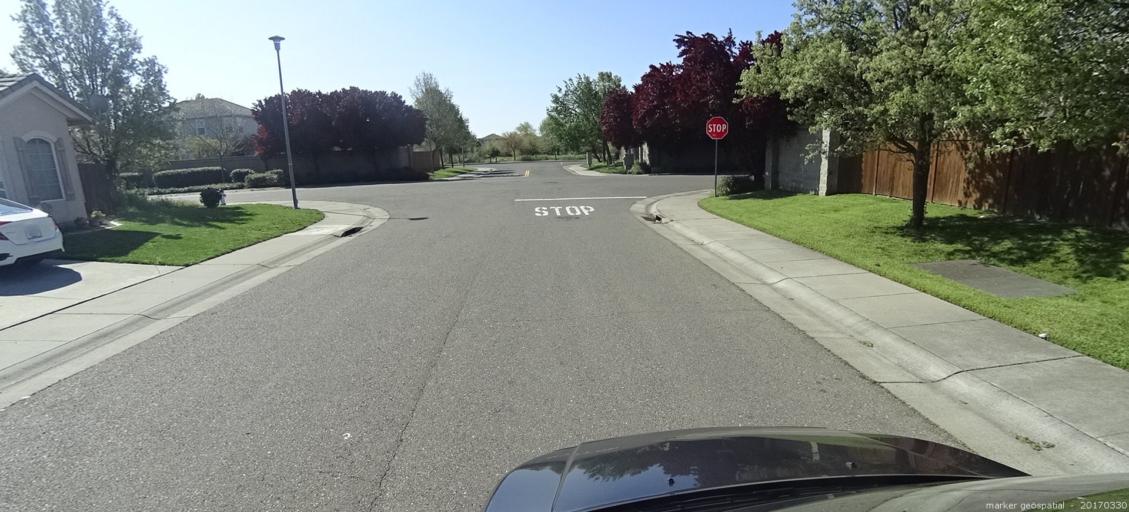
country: US
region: California
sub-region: Sacramento County
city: Laguna
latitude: 38.4437
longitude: -121.4162
